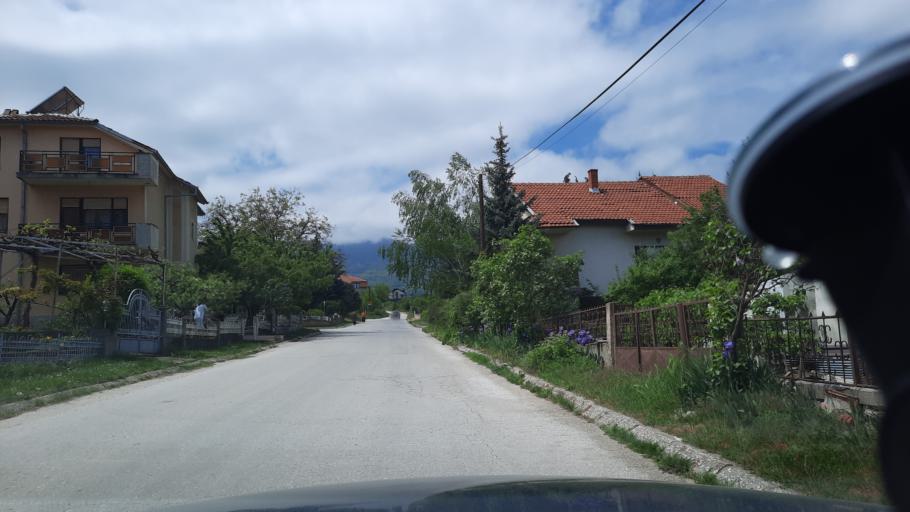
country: MK
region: Bitola
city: Bitola
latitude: 41.0328
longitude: 21.2982
